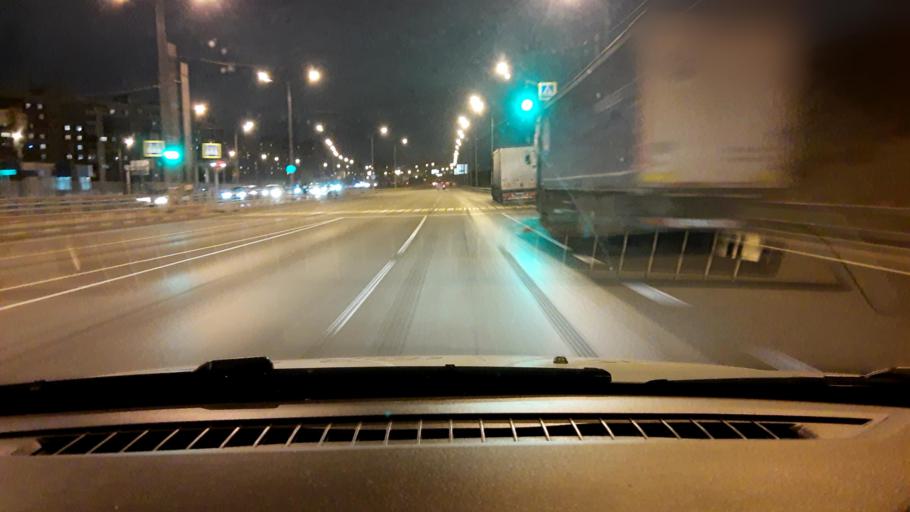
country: RU
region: Nizjnij Novgorod
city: Nizhniy Novgorod
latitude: 56.3463
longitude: 43.9214
